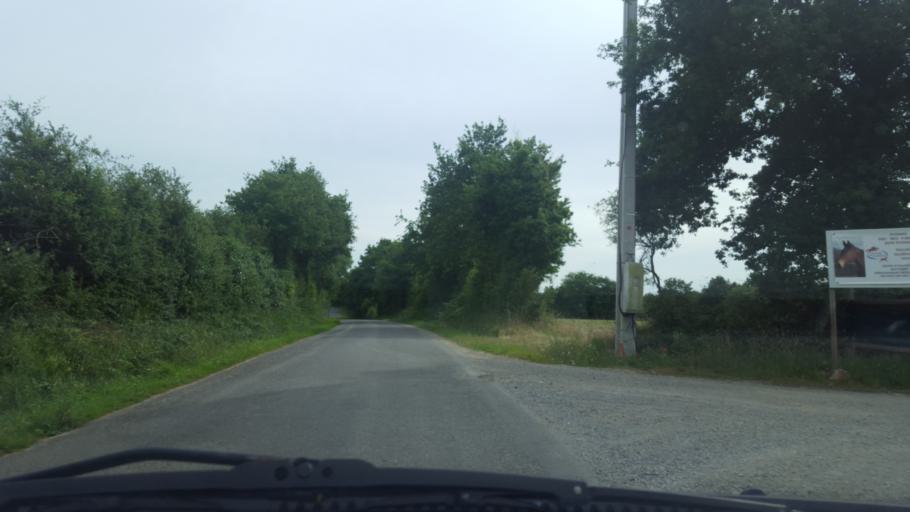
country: FR
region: Pays de la Loire
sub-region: Departement de la Loire-Atlantique
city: La Limouziniere
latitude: 46.9976
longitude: -1.5860
